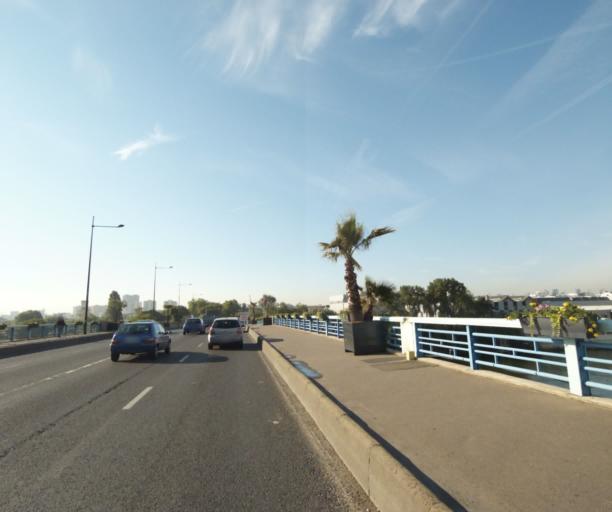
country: FR
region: Ile-de-France
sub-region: Departement du Val-d'Oise
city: Argenteuil
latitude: 48.9402
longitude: 2.2550
